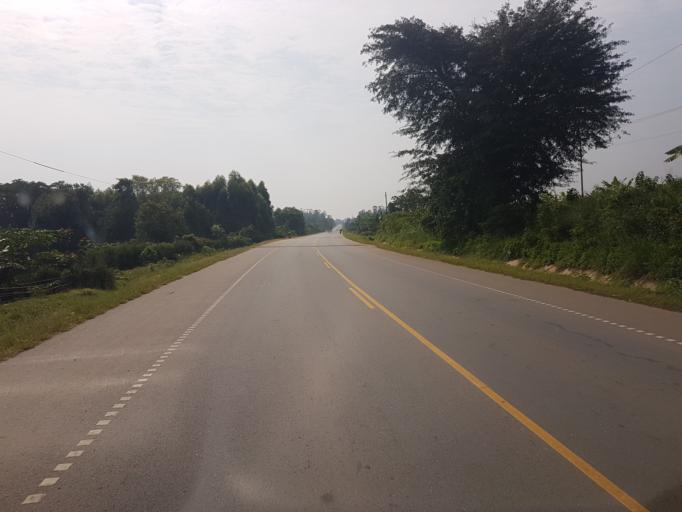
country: UG
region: Western Region
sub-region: Sheema District
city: Kibingo
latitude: -0.6352
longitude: 30.5208
